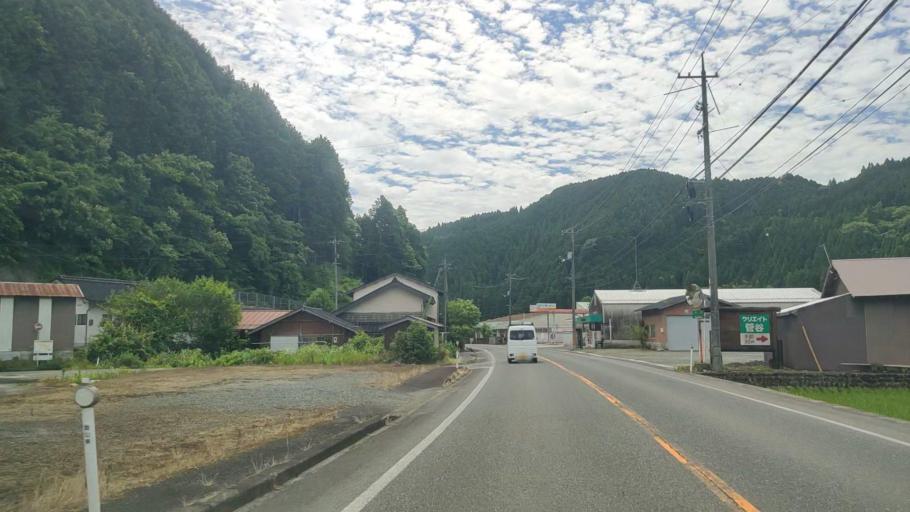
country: JP
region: Okayama
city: Niimi
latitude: 35.1570
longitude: 133.6146
